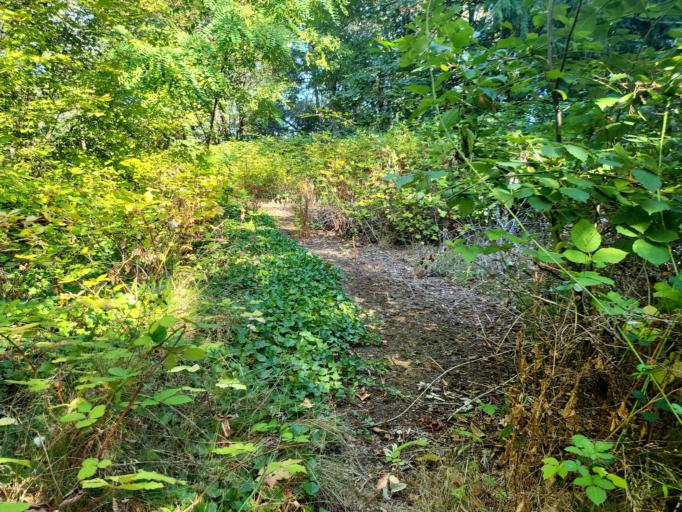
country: US
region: Washington
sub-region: King County
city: Des Moines
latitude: 47.4142
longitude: -122.3100
